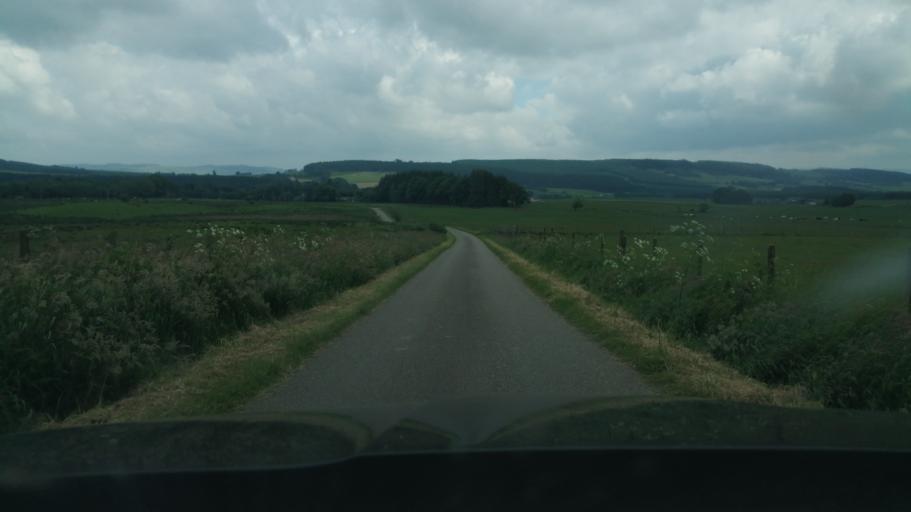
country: GB
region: Scotland
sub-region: Moray
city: Cullen
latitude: 57.5926
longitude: -2.8233
